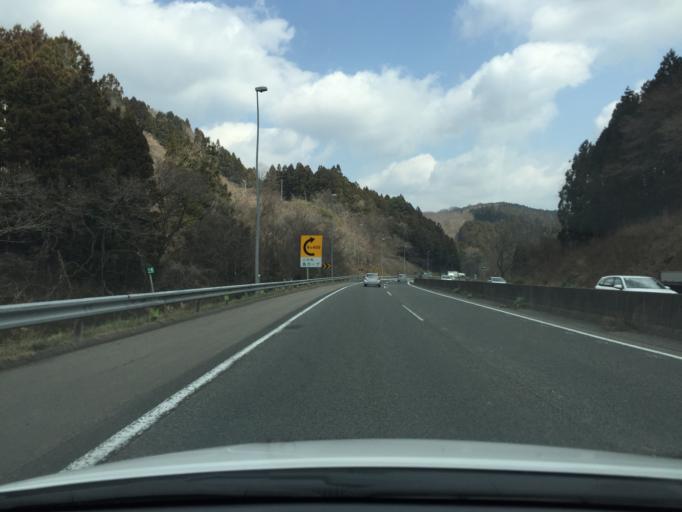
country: JP
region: Miyagi
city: Sendai
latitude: 38.1978
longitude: 140.7851
